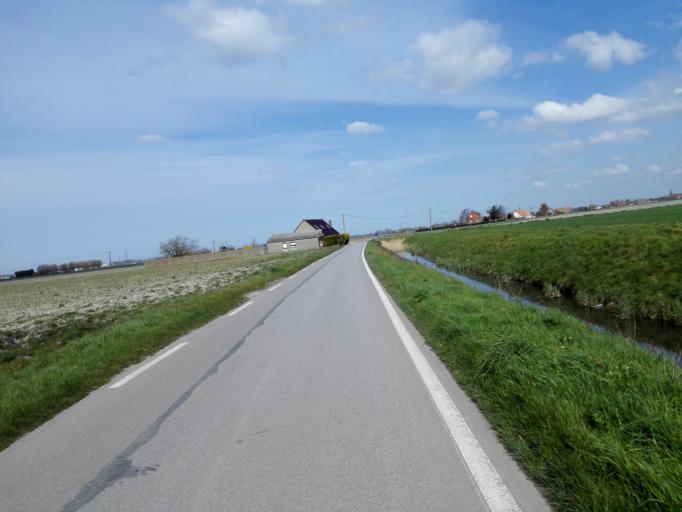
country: FR
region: Nord-Pas-de-Calais
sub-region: Departement du Nord
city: Brouckerque
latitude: 50.9636
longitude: 2.3019
